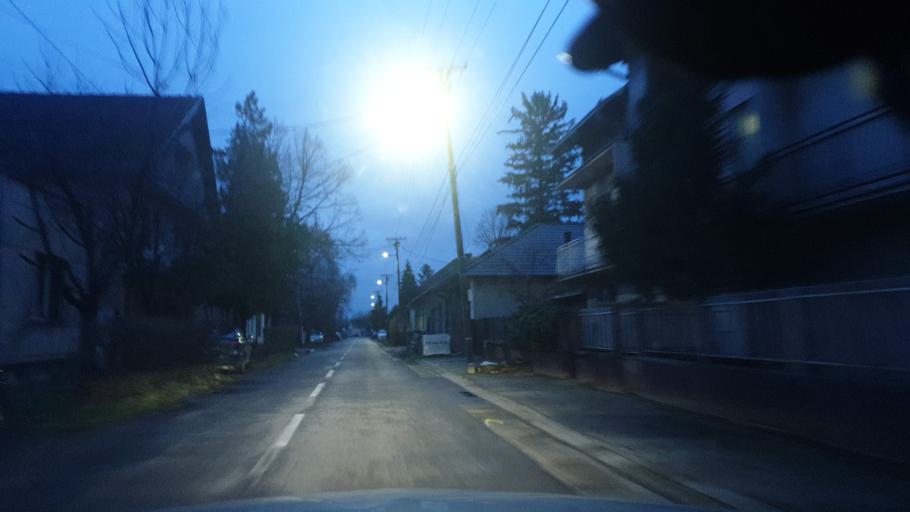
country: RS
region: Autonomna Pokrajina Vojvodina
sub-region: Sremski Okrug
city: Stara Pazova
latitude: 44.9848
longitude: 20.1663
